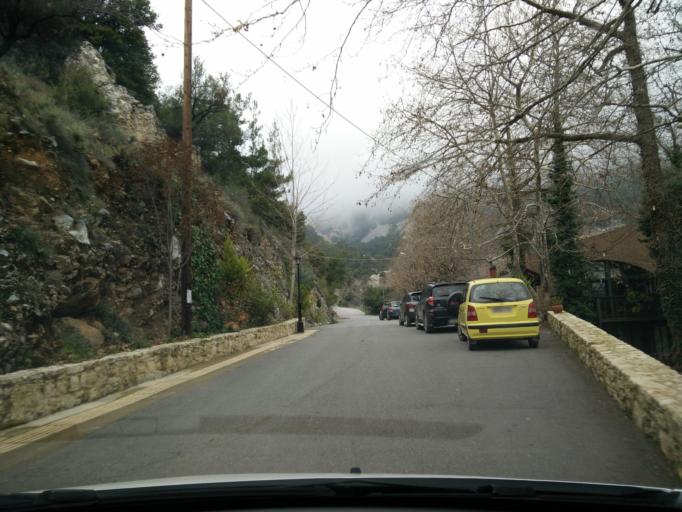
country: GR
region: Crete
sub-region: Nomos Lasithiou
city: Kritsa
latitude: 35.0478
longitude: 25.4892
